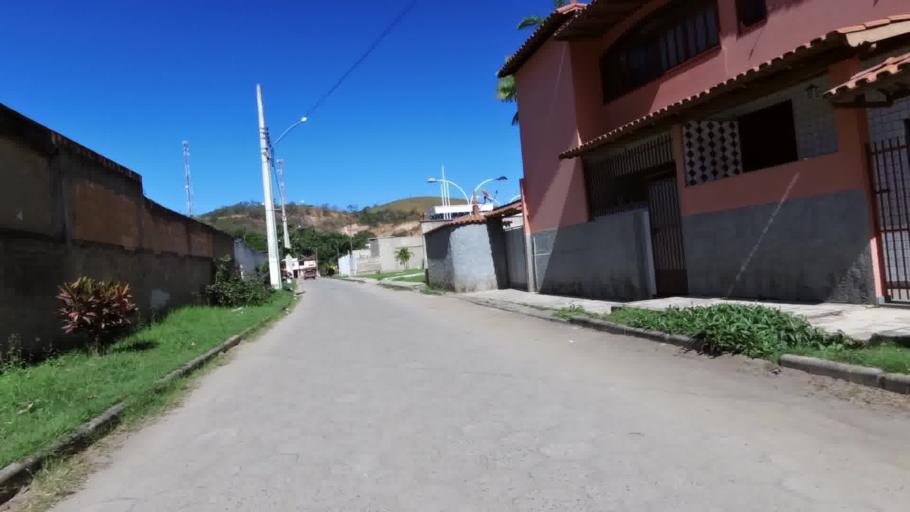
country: BR
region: Espirito Santo
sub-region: Rio Novo Do Sul
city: Rio Novo do Sul
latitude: -20.8640
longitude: -40.9309
